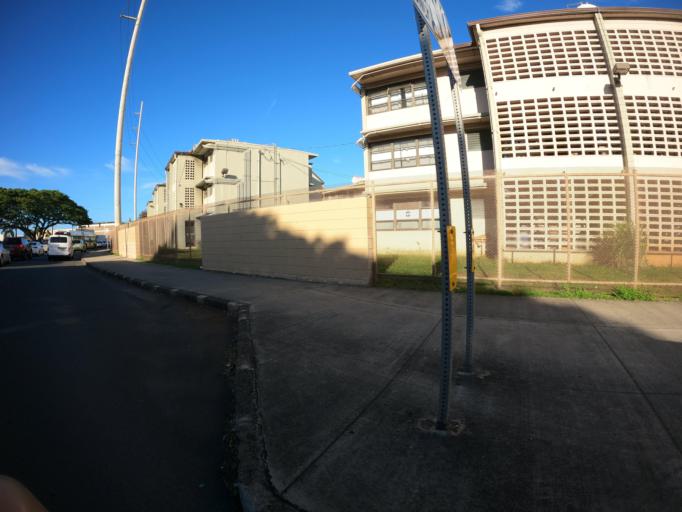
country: US
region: Hawaii
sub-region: Honolulu County
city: Honolulu
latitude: 21.3189
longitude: -157.8637
